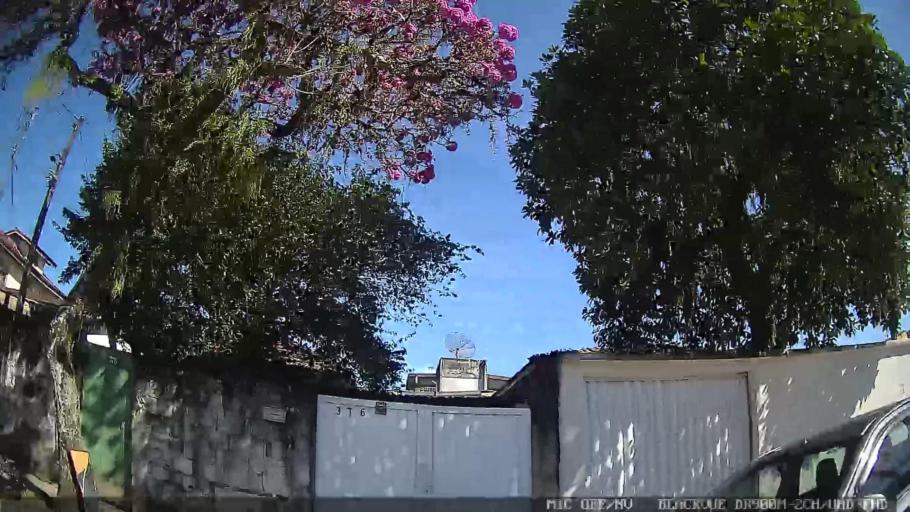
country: BR
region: Sao Paulo
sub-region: Santos
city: Santos
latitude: -23.9423
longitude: -46.2936
